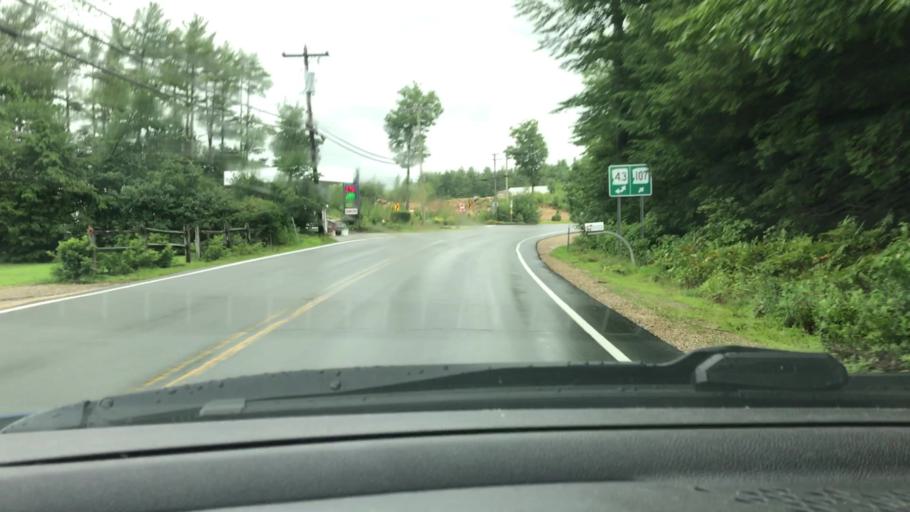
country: US
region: New Hampshire
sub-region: Rockingham County
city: Candia
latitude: 43.1539
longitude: -71.2331
